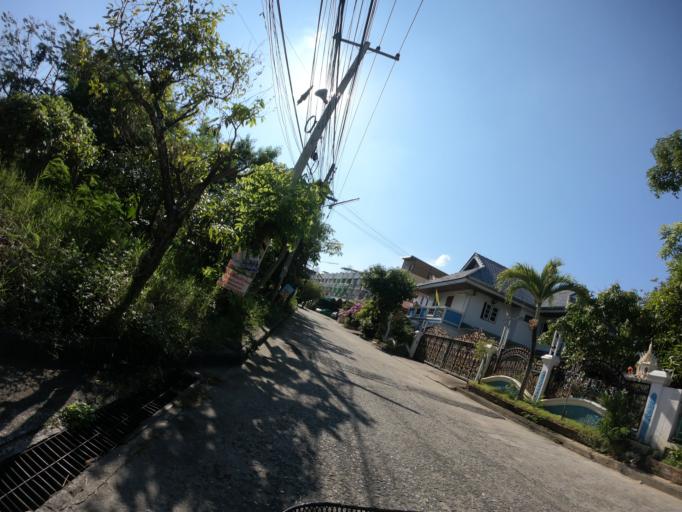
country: TH
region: Chiang Mai
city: Chiang Mai
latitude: 18.7637
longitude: 98.9951
